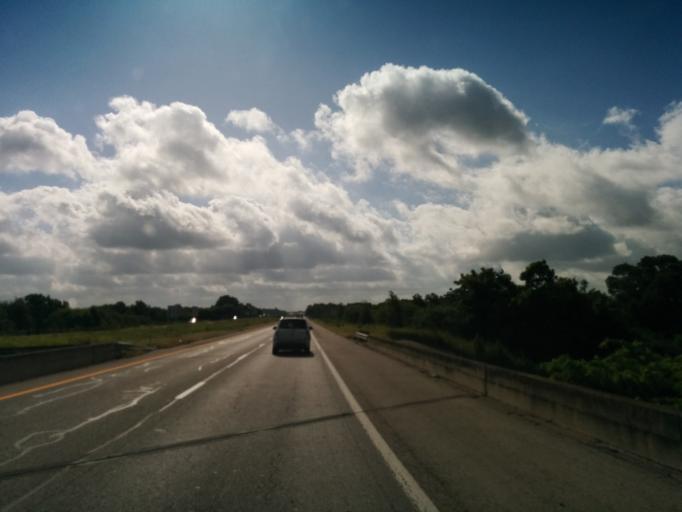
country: US
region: Texas
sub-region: Caldwell County
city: Luling
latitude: 29.6496
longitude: -97.6400
